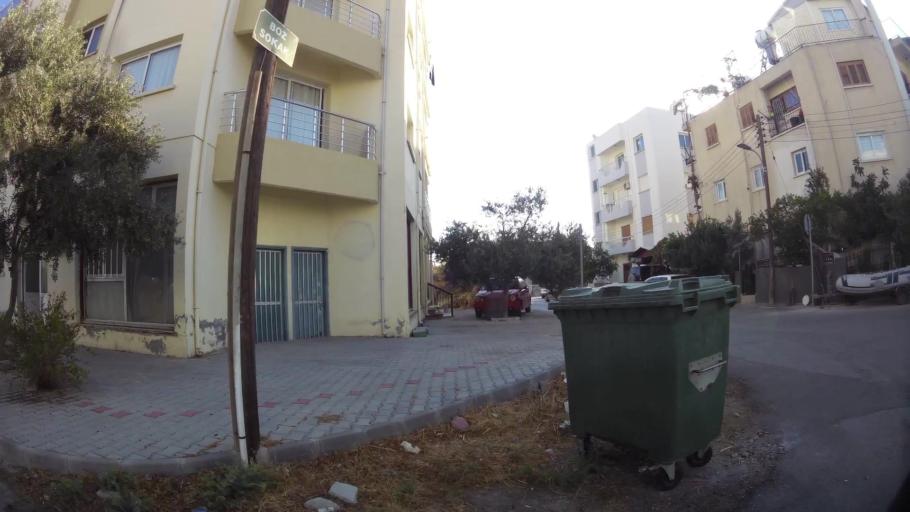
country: CY
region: Lefkosia
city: Nicosia
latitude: 35.2020
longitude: 33.3488
